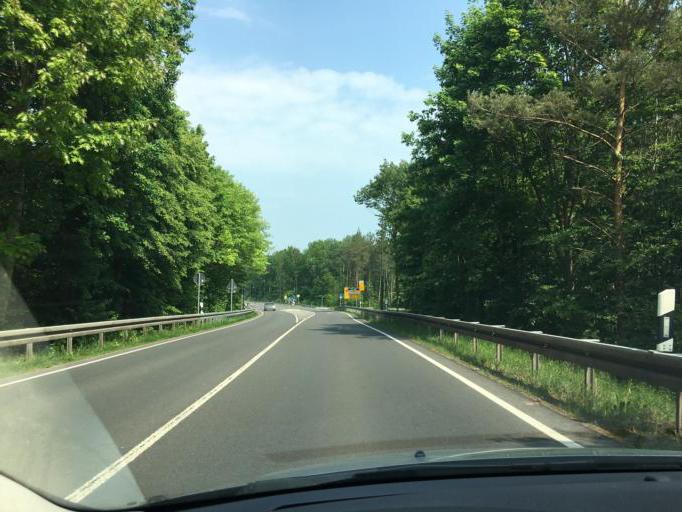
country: DE
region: Saxony
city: Naunhof
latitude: 51.2905
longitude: 12.5892
